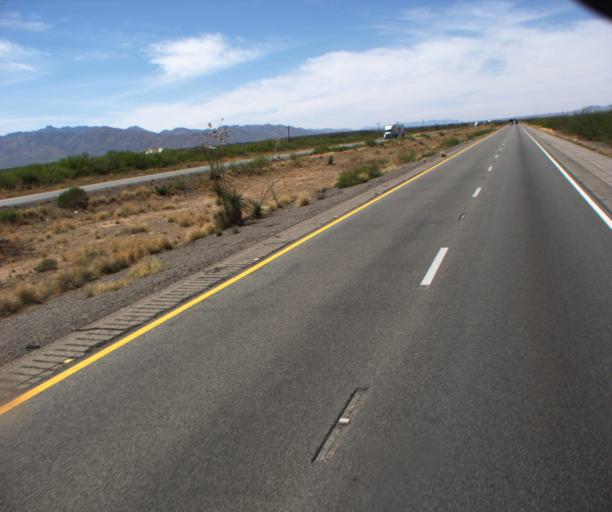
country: US
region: Arizona
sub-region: Cochise County
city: Willcox
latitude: 32.3098
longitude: -109.4080
